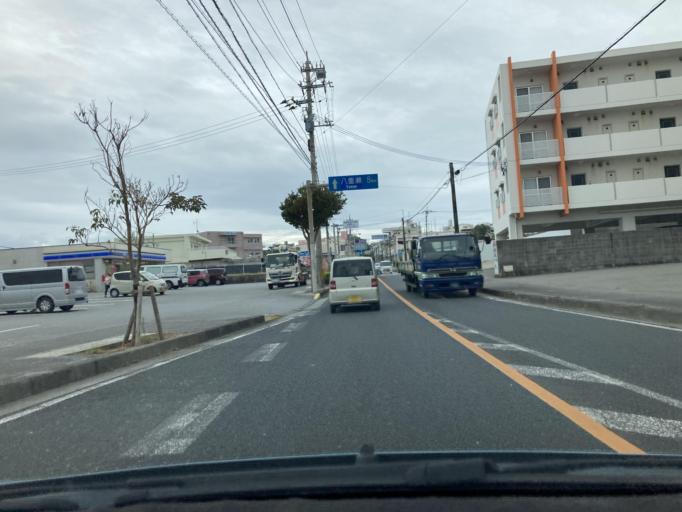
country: JP
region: Okinawa
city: Tomigusuku
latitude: 26.1783
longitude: 127.7183
